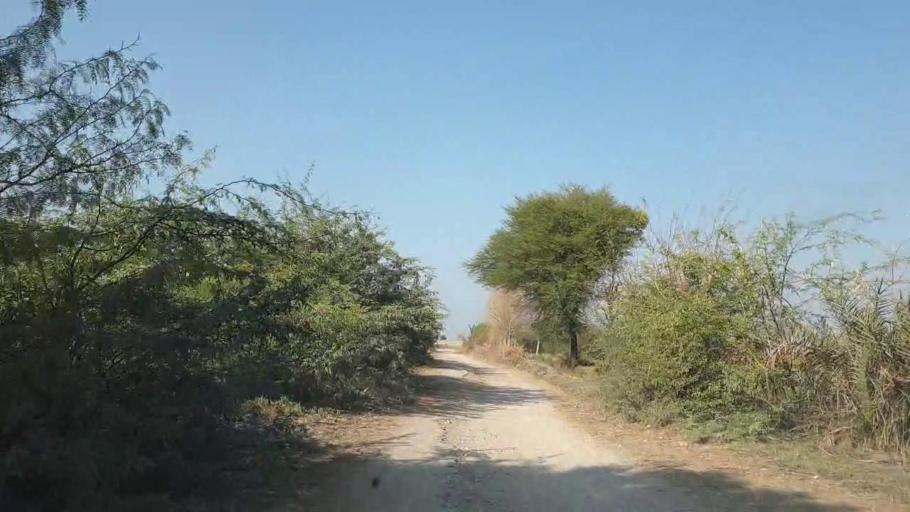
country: PK
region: Sindh
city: Tando Mittha Khan
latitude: 25.7706
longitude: 69.1936
